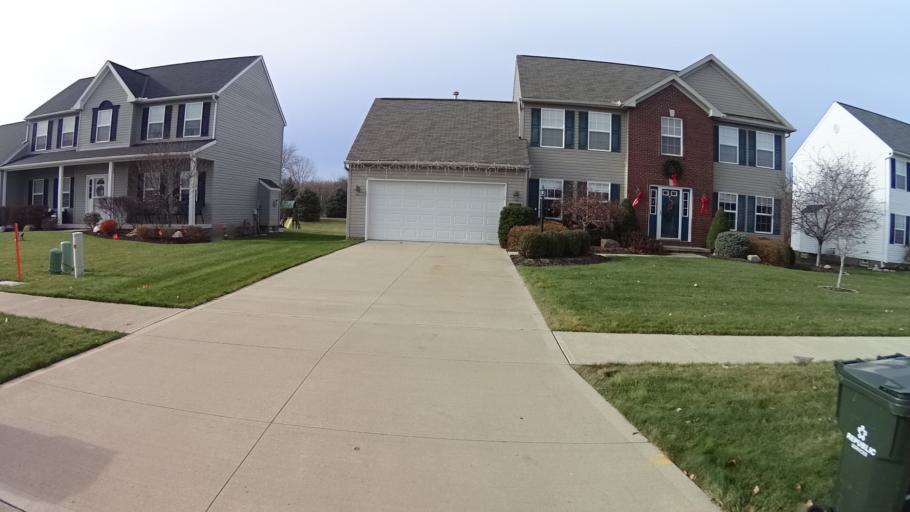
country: US
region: Ohio
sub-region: Lorain County
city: North Ridgeville
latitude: 41.3625
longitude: -82.0540
